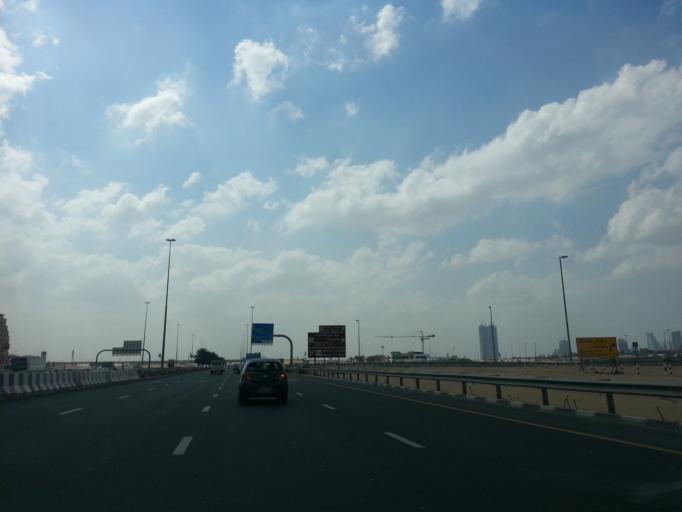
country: AE
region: Ash Shariqah
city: Sharjah
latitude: 25.2164
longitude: 55.3141
